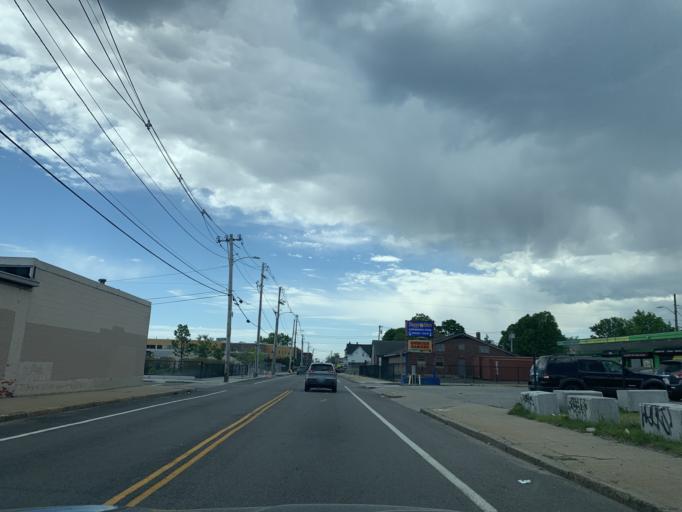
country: US
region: Rhode Island
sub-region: Providence County
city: Providence
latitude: 41.8030
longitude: -71.4067
